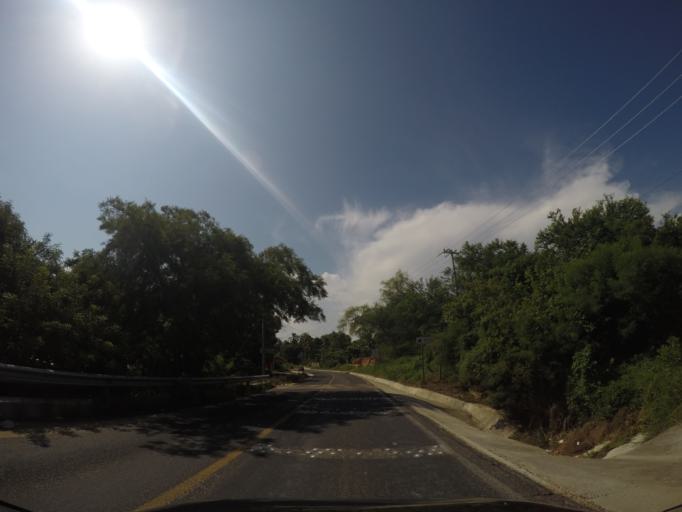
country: MX
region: Oaxaca
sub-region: San Pedro Mixtepec -Dto. 22 -
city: Puerto Escondido
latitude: 15.8821
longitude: -97.1075
